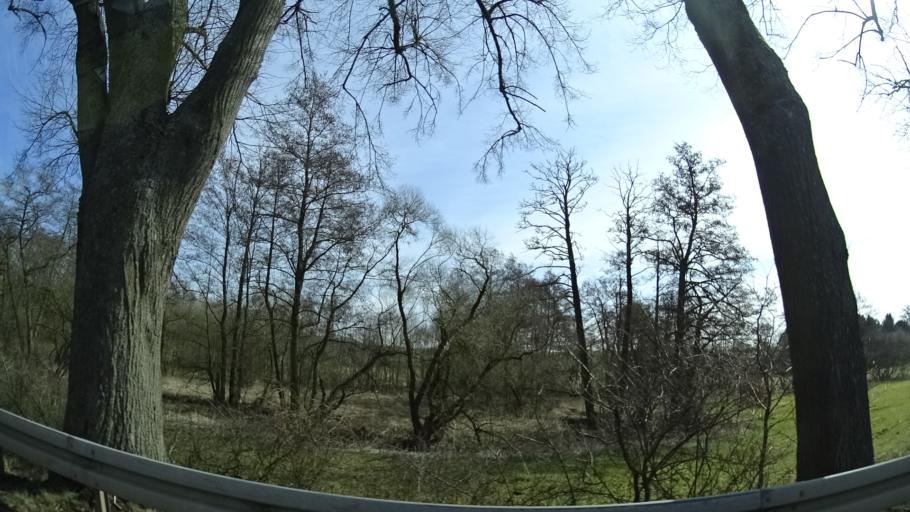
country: DE
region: Hesse
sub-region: Regierungsbezirk Giessen
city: Alsfeld
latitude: 50.6983
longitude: 9.3062
